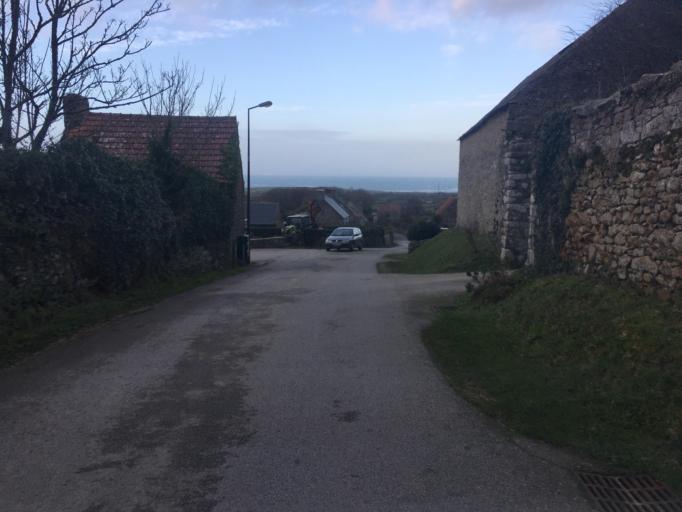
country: FR
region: Lower Normandy
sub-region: Departement de la Manche
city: Beaumont-Hague
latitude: 49.7120
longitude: -1.9221
